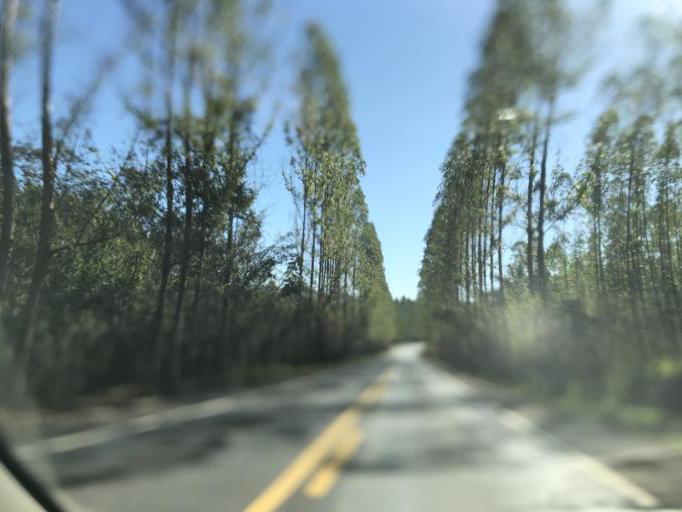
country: BR
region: Minas Gerais
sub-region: Bambui
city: Bambui
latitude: -19.8227
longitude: -46.0152
